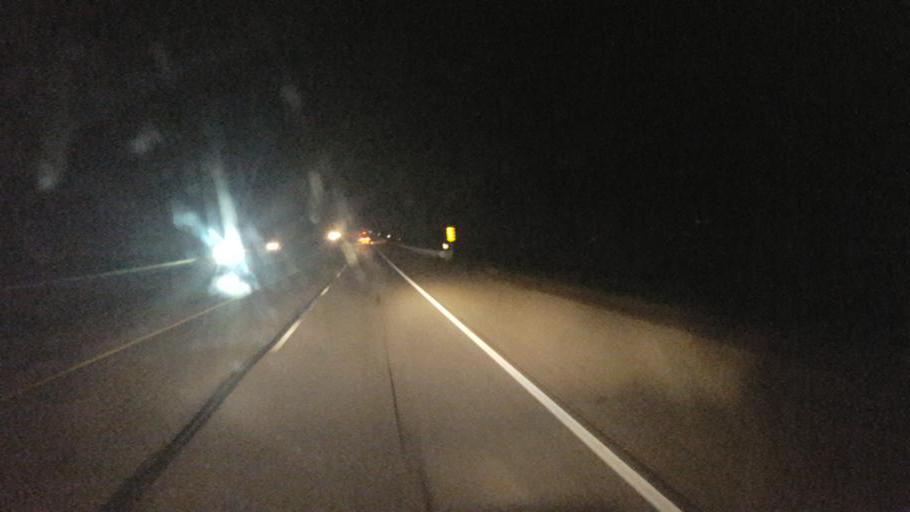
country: US
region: Indiana
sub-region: Wayne County
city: Cambridge City
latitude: 39.8535
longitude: -85.1986
